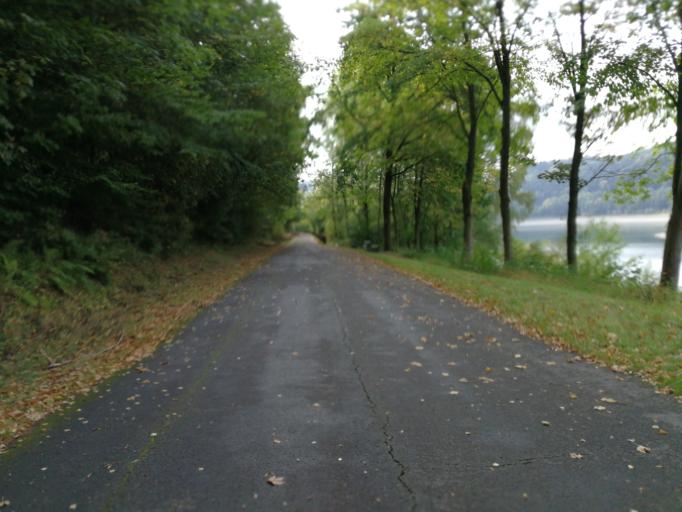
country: DE
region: North Rhine-Westphalia
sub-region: Regierungsbezirk Arnsberg
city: Meschede
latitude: 51.3306
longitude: 8.2672
